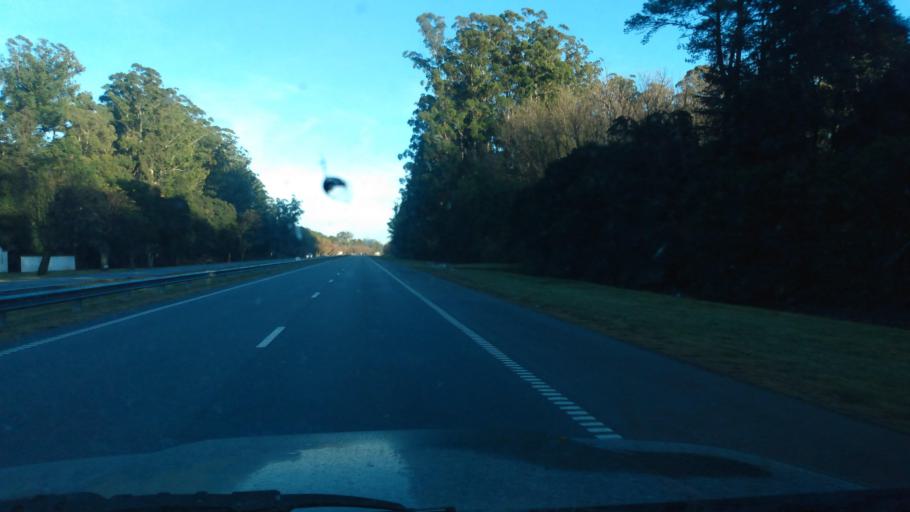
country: AR
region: Buenos Aires
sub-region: Partido de Lujan
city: Lujan
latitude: -34.5437
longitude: -59.2321
